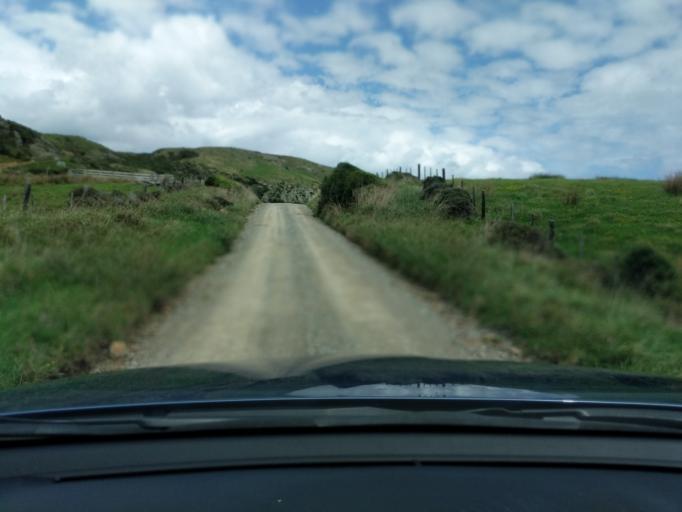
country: NZ
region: Tasman
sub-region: Tasman District
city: Takaka
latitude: -40.6608
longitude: 172.4118
